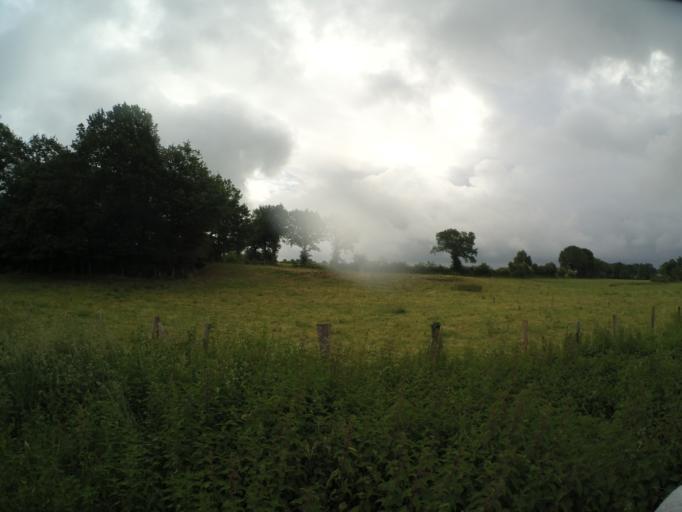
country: FR
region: Pays de la Loire
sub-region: Departement de la Vendee
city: Nesmy
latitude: 46.6135
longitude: -1.4002
